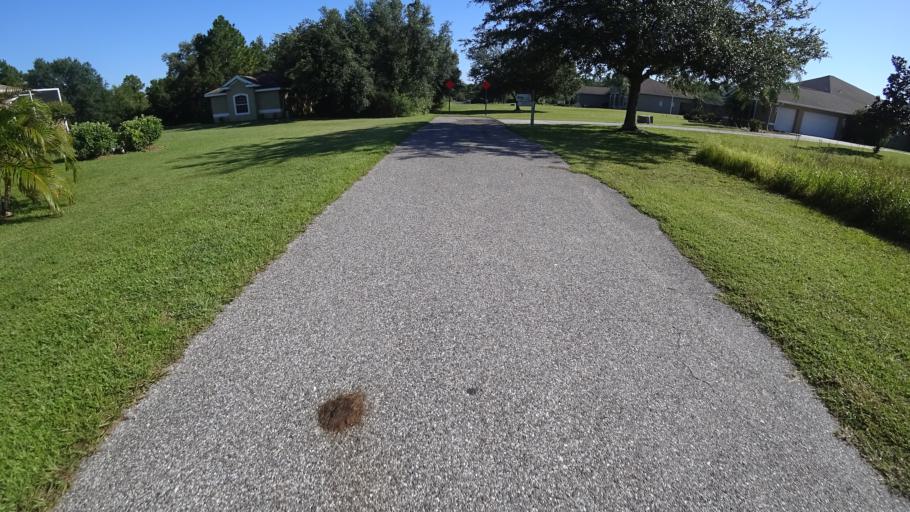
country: US
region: Florida
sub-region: Sarasota County
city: The Meadows
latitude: 27.4041
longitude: -82.3108
